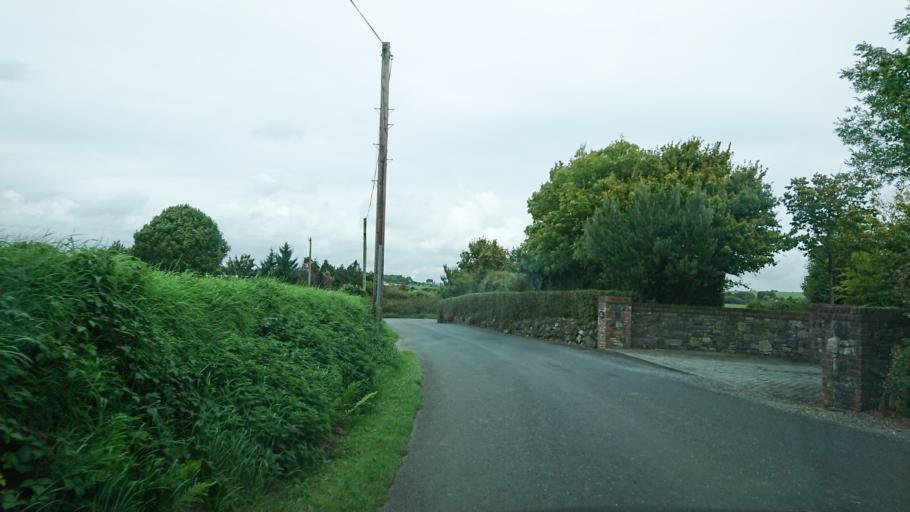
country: IE
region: Munster
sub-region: Waterford
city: Waterford
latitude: 52.2169
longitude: -7.0408
